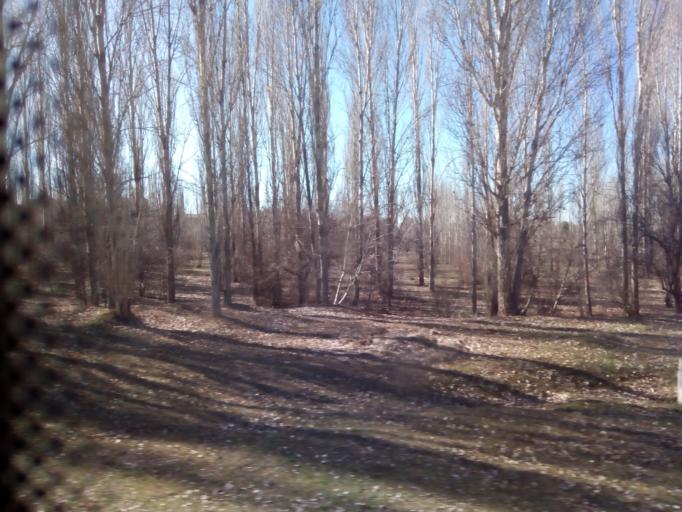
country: TR
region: Ankara
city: Ankara
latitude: 39.8916
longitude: 32.7772
